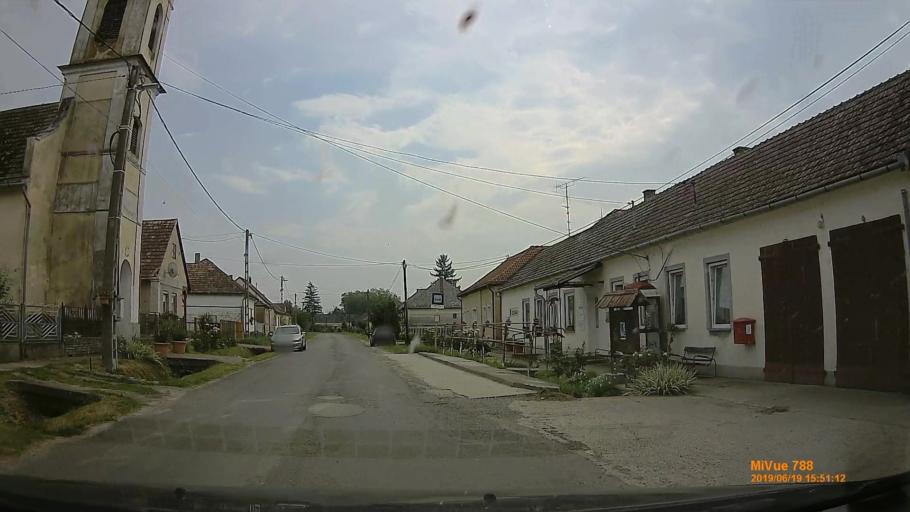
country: HU
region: Baranya
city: Szigetvar
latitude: 46.0296
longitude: 17.7447
